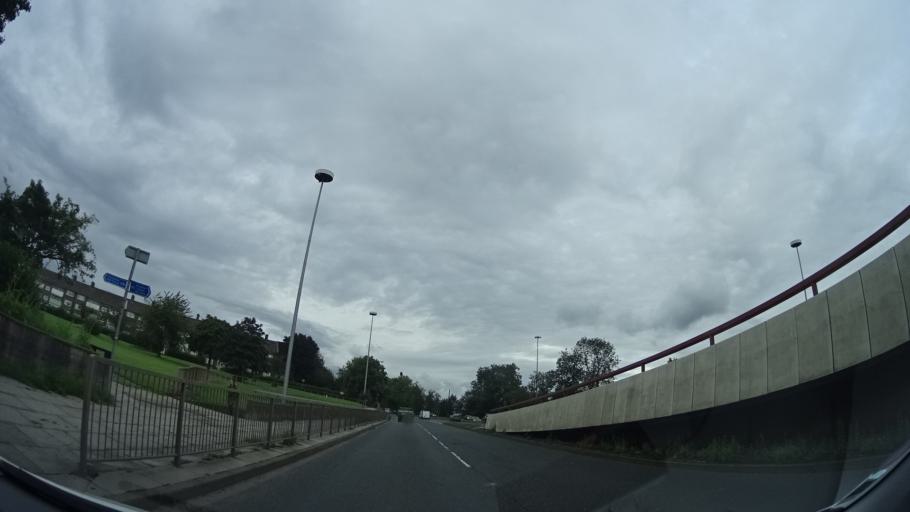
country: GB
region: England
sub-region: Knowsley
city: Huyton
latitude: 53.4089
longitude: -2.9018
